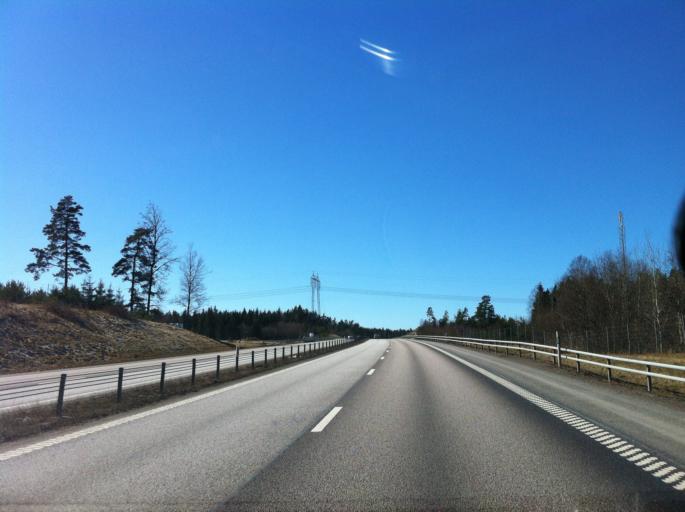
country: SE
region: Vaestra Goetaland
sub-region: Vanersborgs Kommun
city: Vanersborg
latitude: 58.3764
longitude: 12.3395
